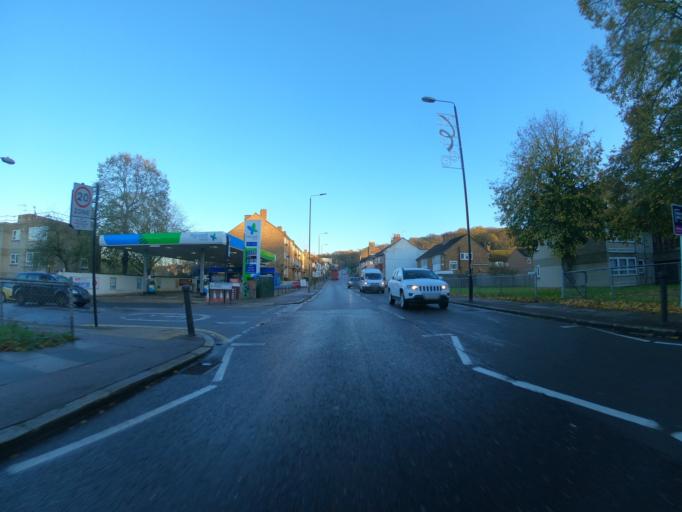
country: GB
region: England
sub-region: Greater London
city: Abbey Wood
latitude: 51.4852
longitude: 0.1043
